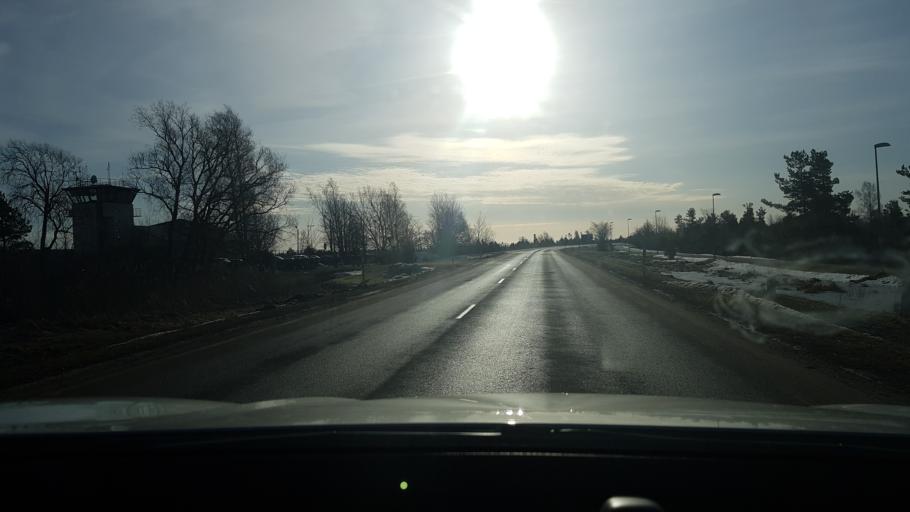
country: EE
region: Saare
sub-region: Kuressaare linn
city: Kuressaare
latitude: 58.2329
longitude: 22.5027
